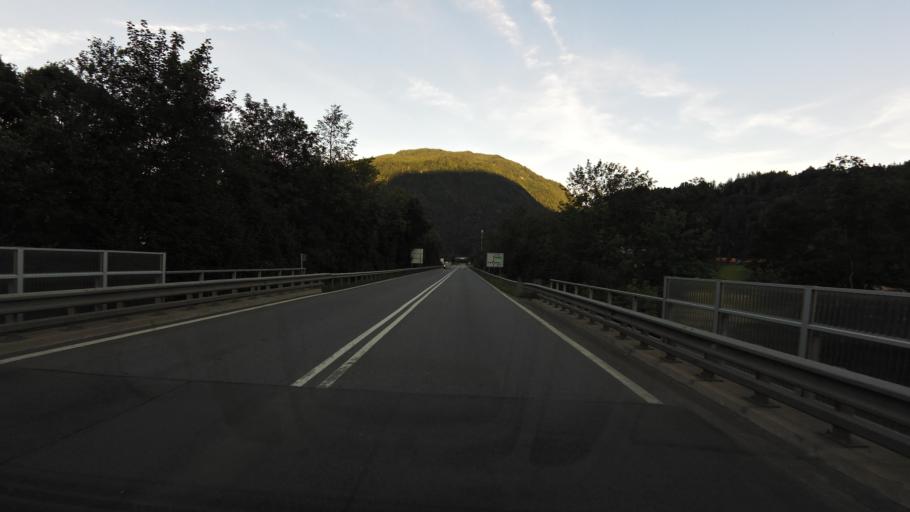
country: AT
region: Tyrol
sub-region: Politischer Bezirk Kufstein
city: Schwoich
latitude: 47.5685
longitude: 12.1454
